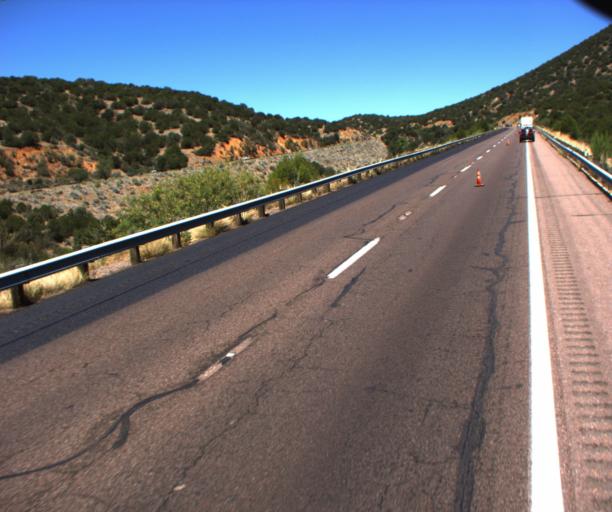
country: US
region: Arizona
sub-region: Gila County
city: Payson
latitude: 34.1594
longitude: -111.3210
